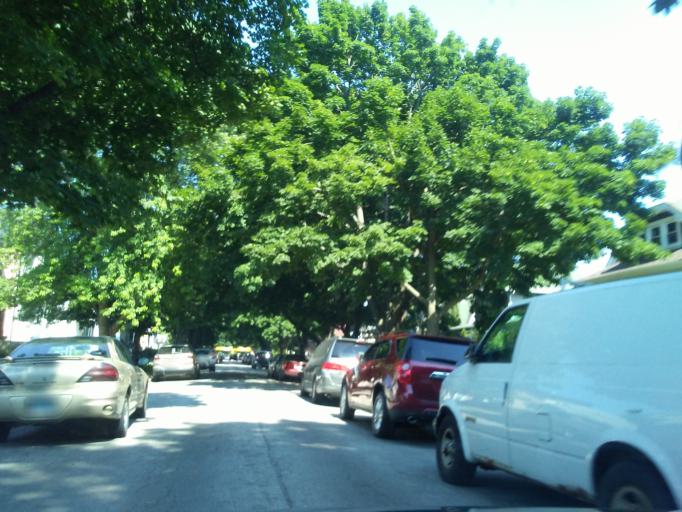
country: US
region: Illinois
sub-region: Cook County
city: Lincolnwood
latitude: 41.9716
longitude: -87.7546
